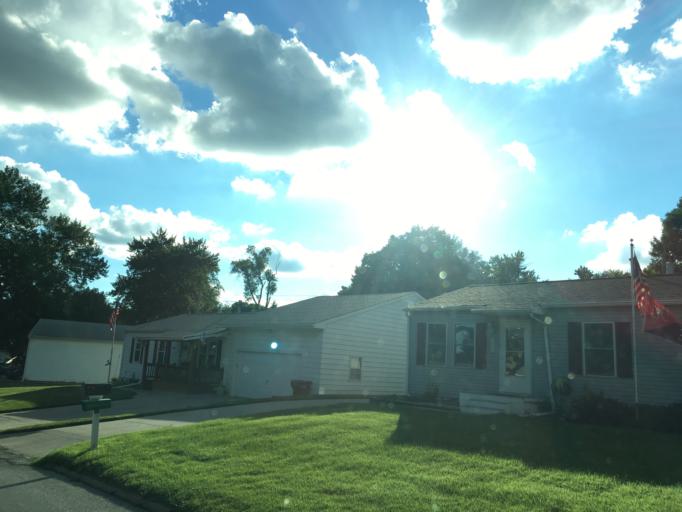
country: US
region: Nebraska
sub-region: Sarpy County
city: La Vista
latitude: 41.1828
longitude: -95.9741
